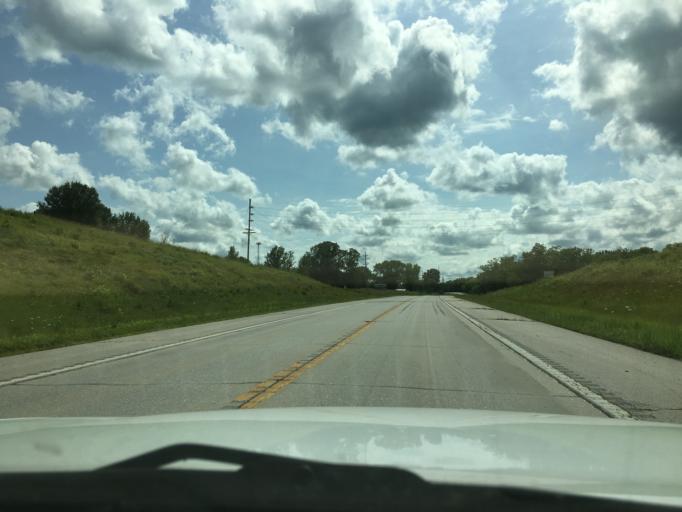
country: US
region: Missouri
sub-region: Franklin County
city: Gerald
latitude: 38.4121
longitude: -91.3099
